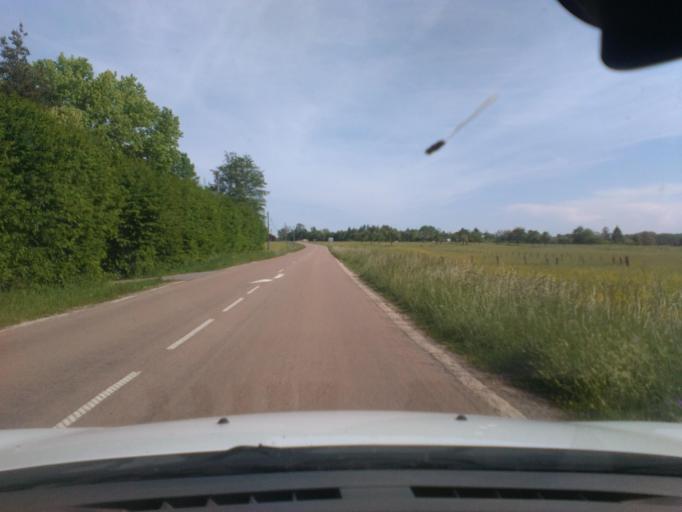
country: FR
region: Lorraine
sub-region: Departement des Vosges
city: Rambervillers
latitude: 48.3680
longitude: 6.6172
